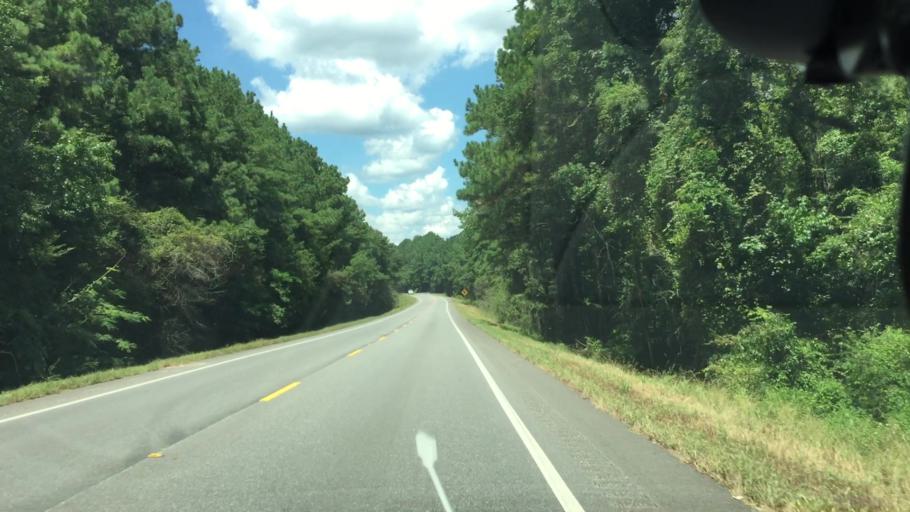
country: US
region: Alabama
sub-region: Coffee County
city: New Brockton
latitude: 31.4609
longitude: -85.8986
